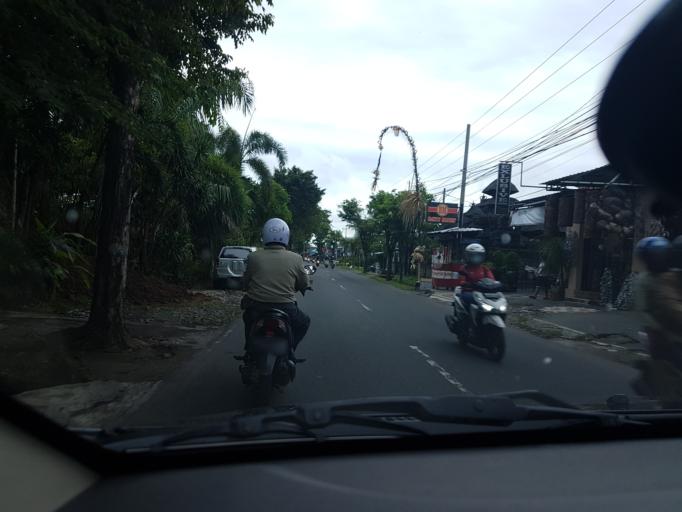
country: ID
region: Bali
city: Banjar Gunungpande
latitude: -8.6544
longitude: 115.1677
